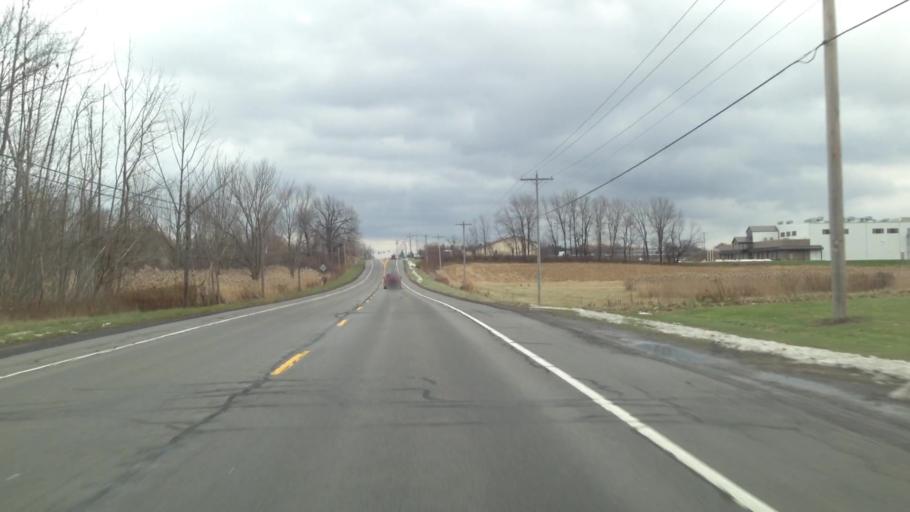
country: US
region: New York
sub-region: Erie County
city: Akron
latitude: 42.9929
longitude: -78.4143
